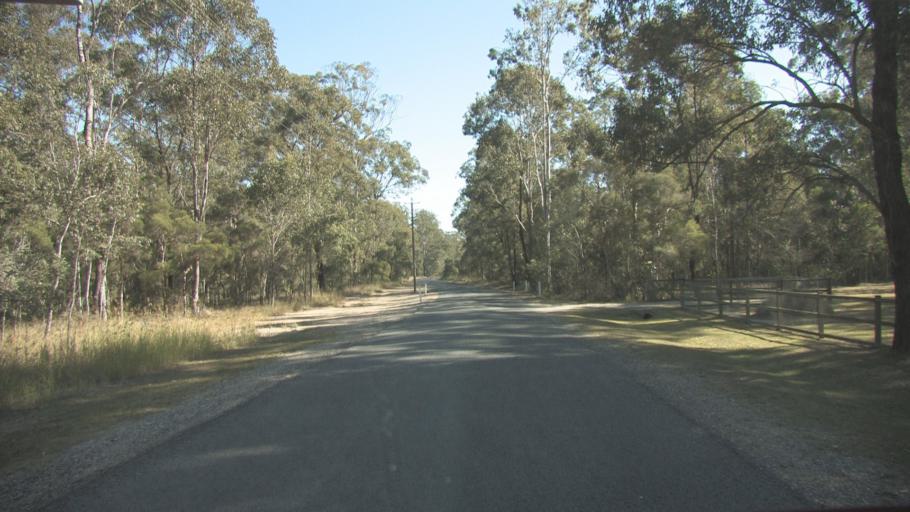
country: AU
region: Queensland
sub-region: Logan
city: Chambers Flat
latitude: -27.7811
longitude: 153.1298
